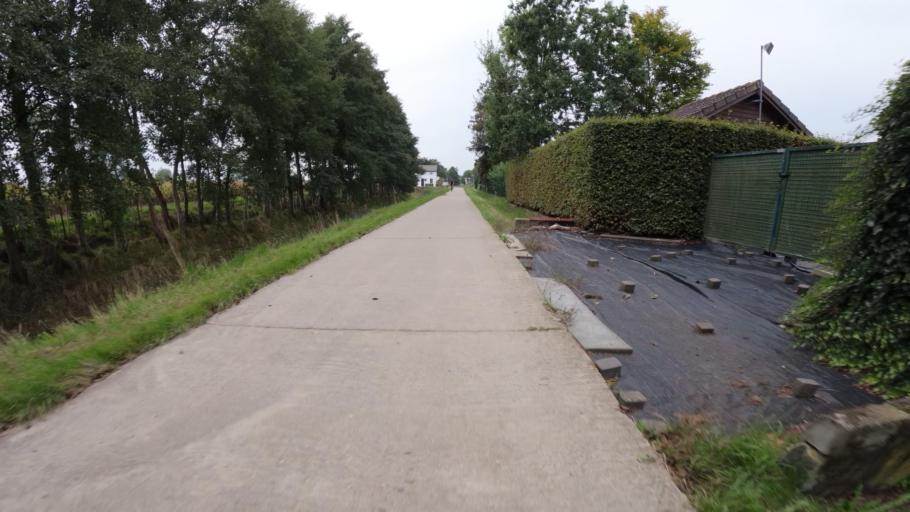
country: BE
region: Flanders
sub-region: Provincie Oost-Vlaanderen
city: Sint-Gillis-Waas
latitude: 51.2197
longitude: 4.0920
